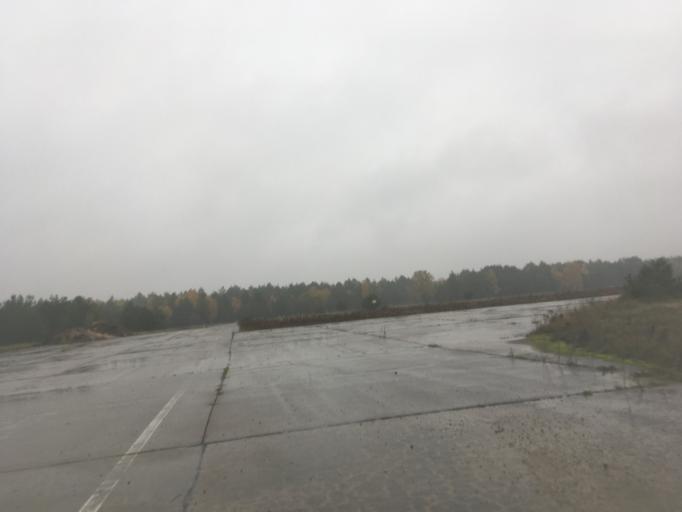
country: DE
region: Brandenburg
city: Halbe
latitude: 52.0361
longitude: 13.7292
